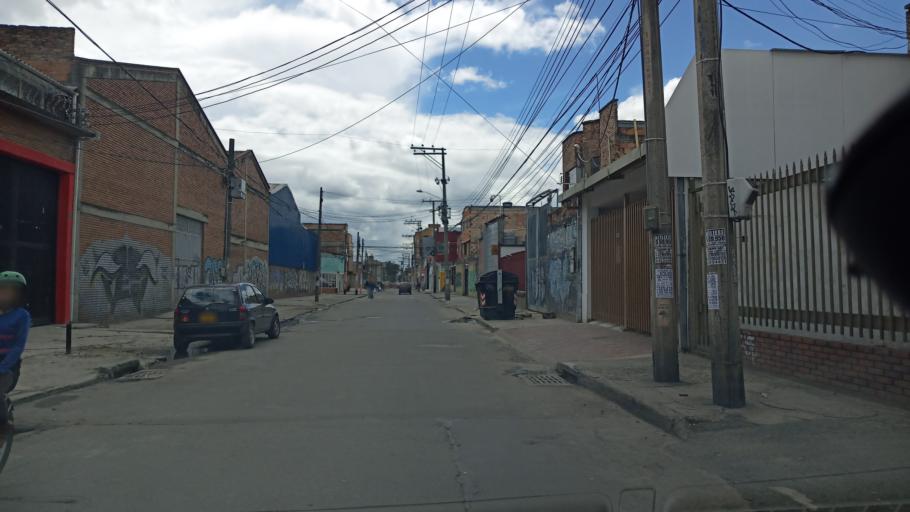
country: CO
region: Cundinamarca
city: Funza
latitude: 4.6726
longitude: -74.1420
